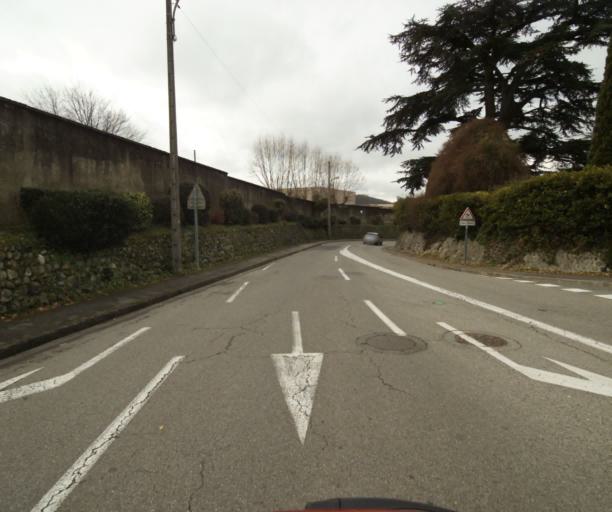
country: FR
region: Midi-Pyrenees
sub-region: Departement de l'Ariege
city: Pamiers
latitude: 43.1144
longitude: 1.6197
